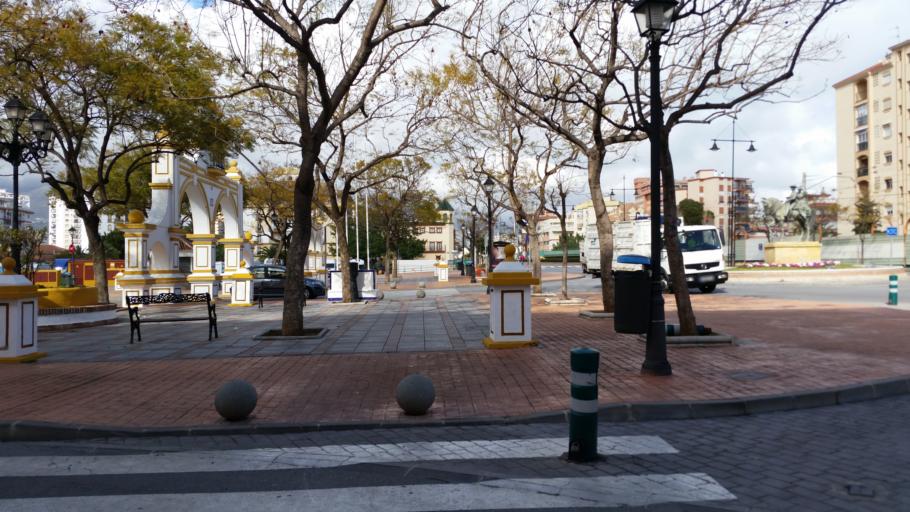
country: ES
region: Andalusia
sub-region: Provincia de Malaga
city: Fuengirola
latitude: 36.5480
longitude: -4.6198
